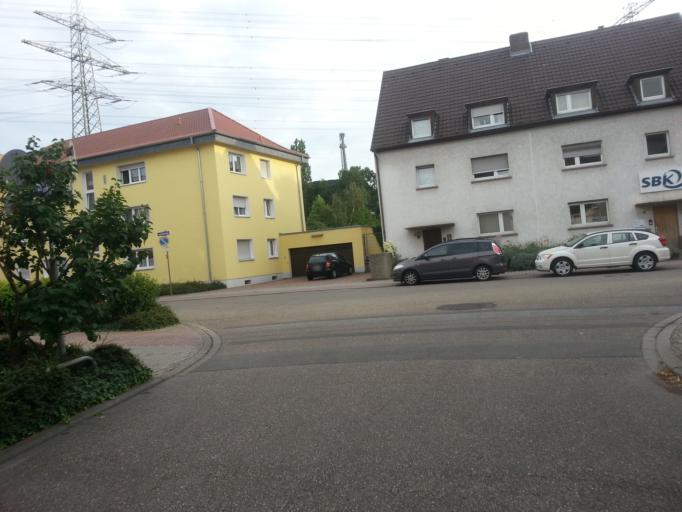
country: DE
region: Rheinland-Pfalz
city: Altrip
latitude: 49.4468
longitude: 8.4949
